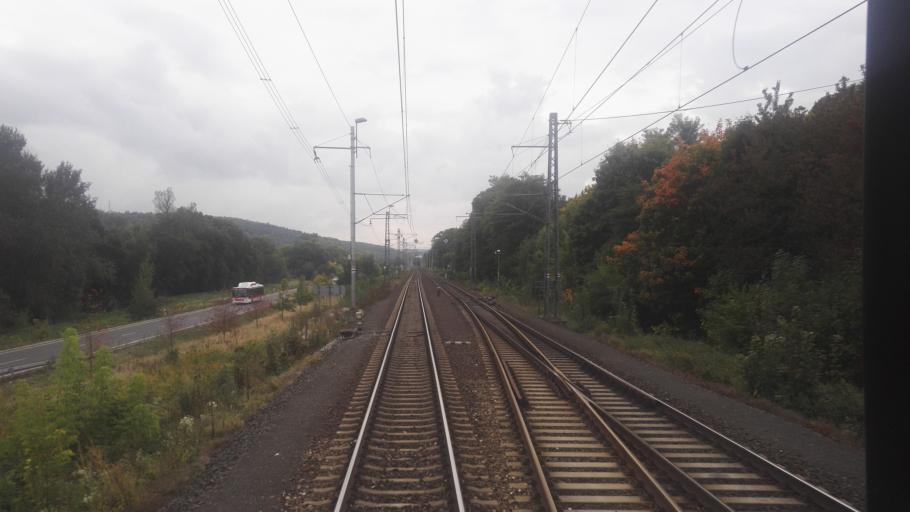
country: CZ
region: Central Bohemia
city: Roztoky
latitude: 50.1522
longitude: 14.3977
